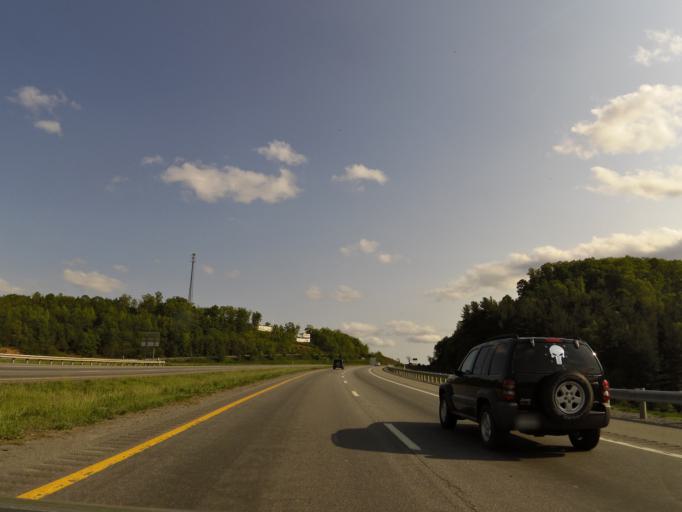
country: US
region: West Virginia
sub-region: Mercer County
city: Princeton
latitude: 37.3367
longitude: -81.1285
